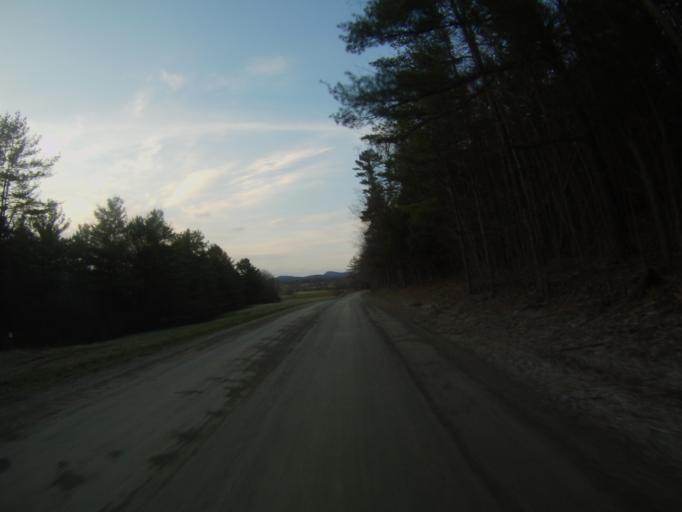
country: US
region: Vermont
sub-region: Addison County
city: Middlebury (village)
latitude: 44.0273
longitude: -73.2206
